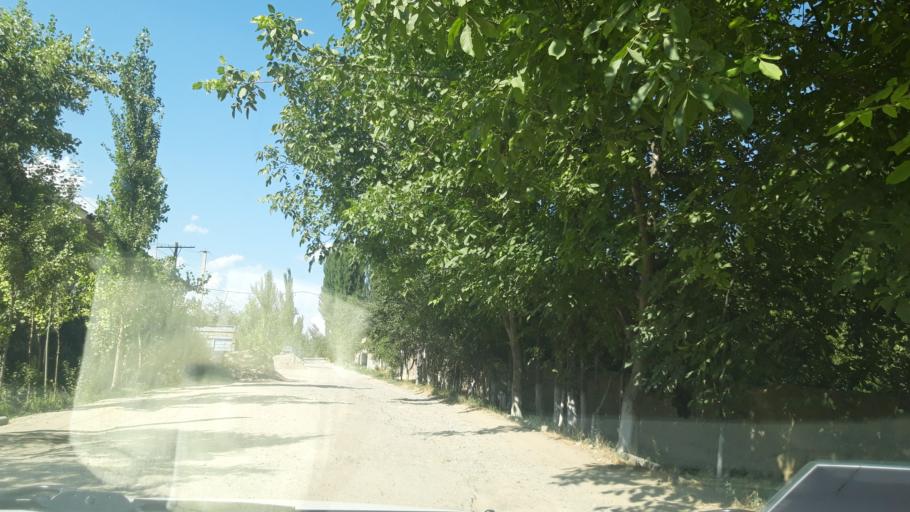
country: UZ
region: Namangan
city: Yangiqo`rg`on
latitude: 41.2151
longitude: 71.7146
